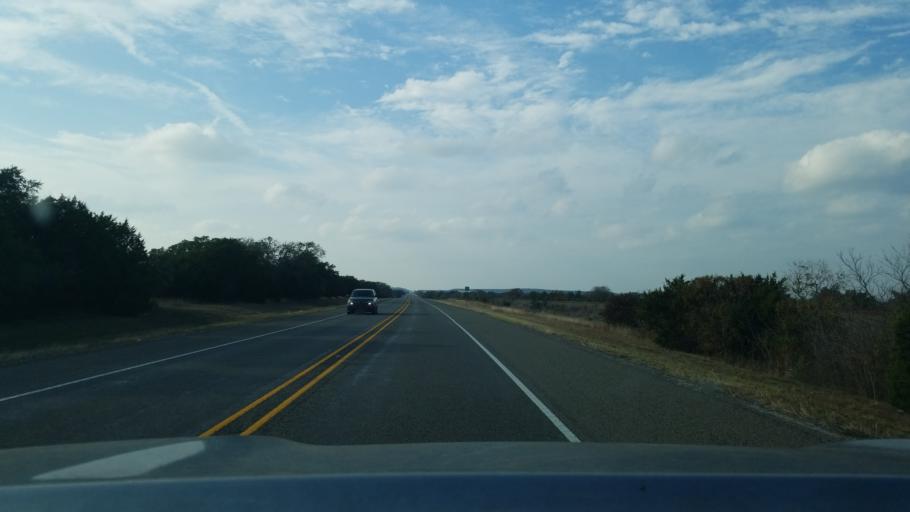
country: US
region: Texas
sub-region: Lampasas County
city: Lampasas
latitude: 31.1655
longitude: -98.3372
